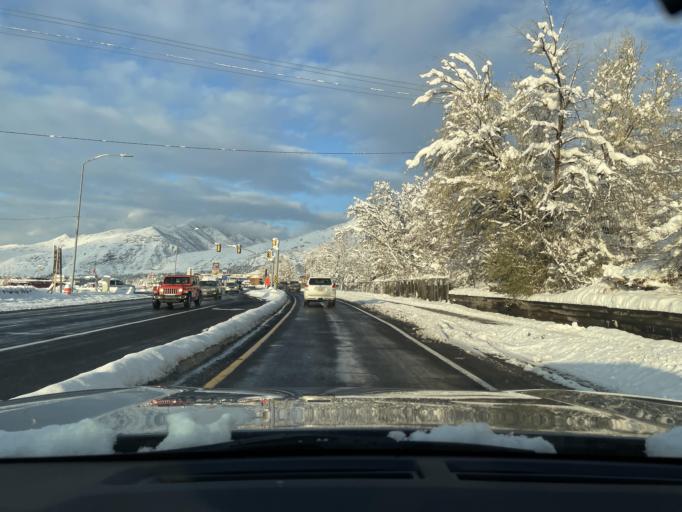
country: US
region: Utah
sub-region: Salt Lake County
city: Mount Olympus
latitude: 40.6819
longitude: -111.7966
